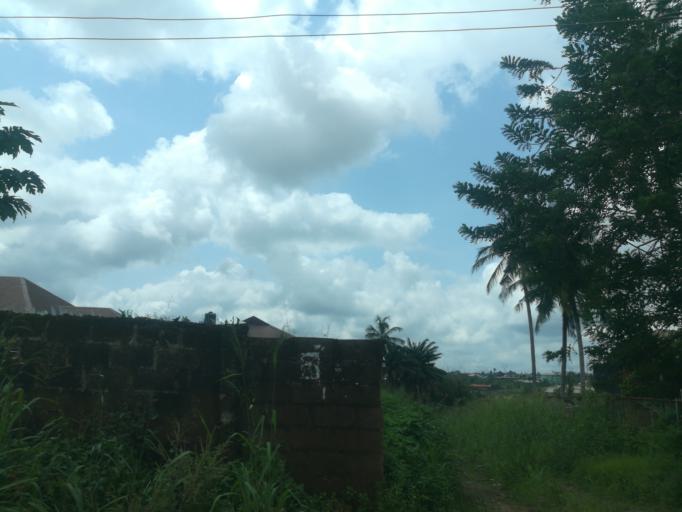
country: NG
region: Oyo
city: Ibadan
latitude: 7.3671
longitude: 3.8265
